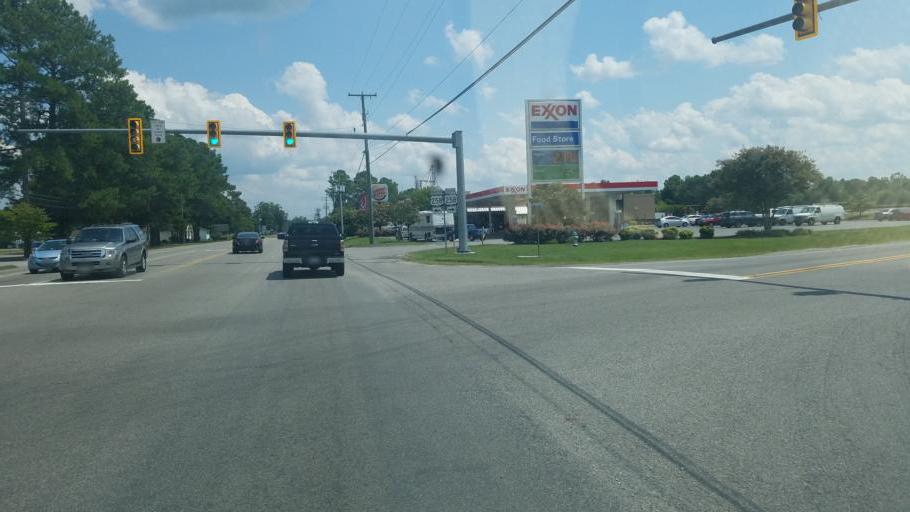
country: US
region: Virginia
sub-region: Isle of Wight County
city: Windsor
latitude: 36.8126
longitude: -76.7507
